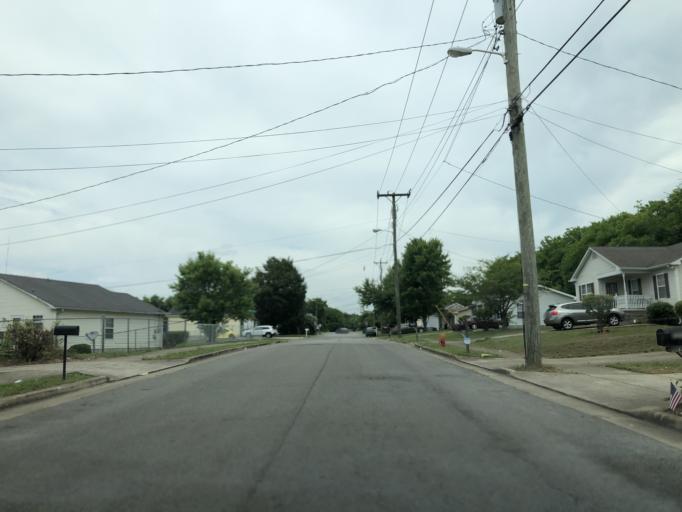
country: US
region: Tennessee
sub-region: Davidson County
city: Nashville
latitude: 36.2442
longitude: -86.7732
